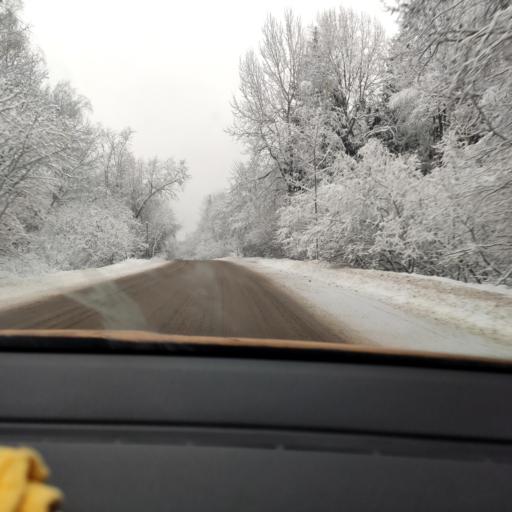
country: RU
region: Moskovskaya
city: Yershovo
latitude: 55.8113
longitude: 36.8942
